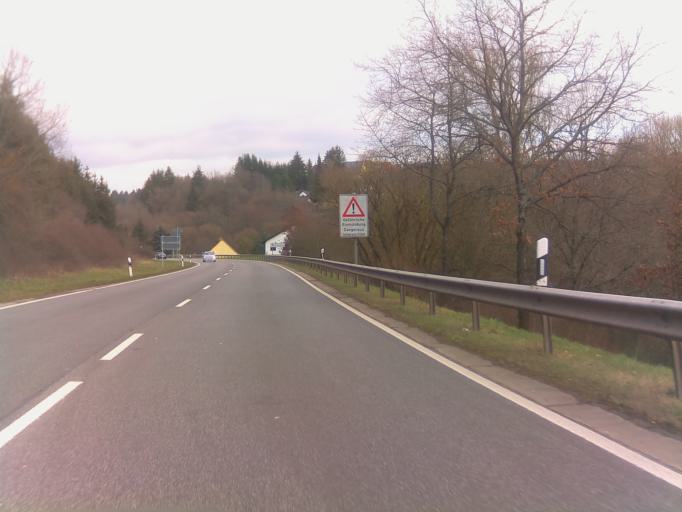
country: DE
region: Rheinland-Pfalz
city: Ruschberg
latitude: 49.6240
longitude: 7.2832
